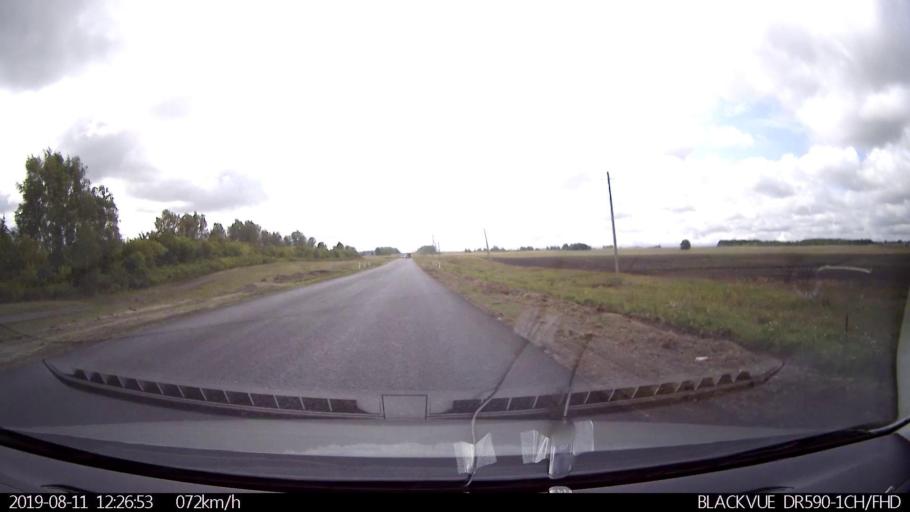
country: RU
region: Ulyanovsk
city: Ignatovka
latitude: 53.8610
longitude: 47.9281
